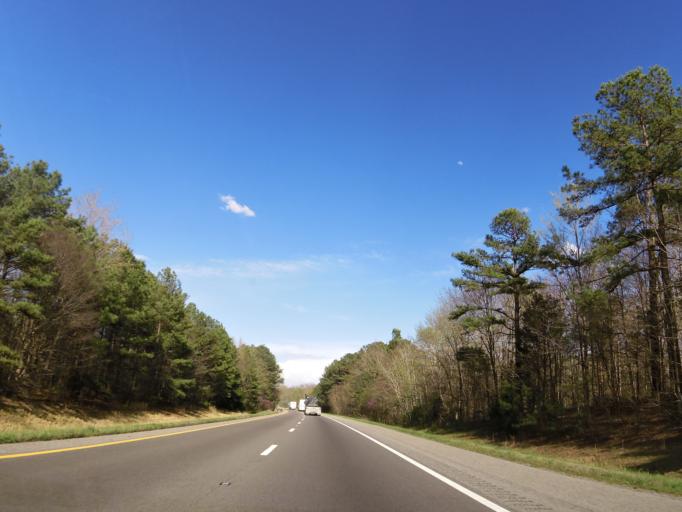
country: US
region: Tennessee
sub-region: Dickson County
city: Dickson
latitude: 36.0090
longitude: -87.3876
